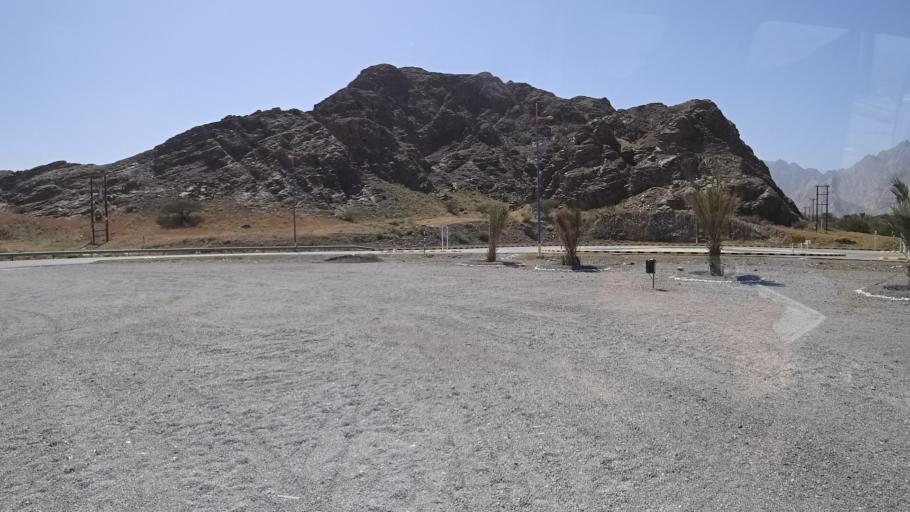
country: OM
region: Muhafazat ad Dakhiliyah
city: Sufalat Sama'il
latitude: 23.3430
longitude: 58.0137
